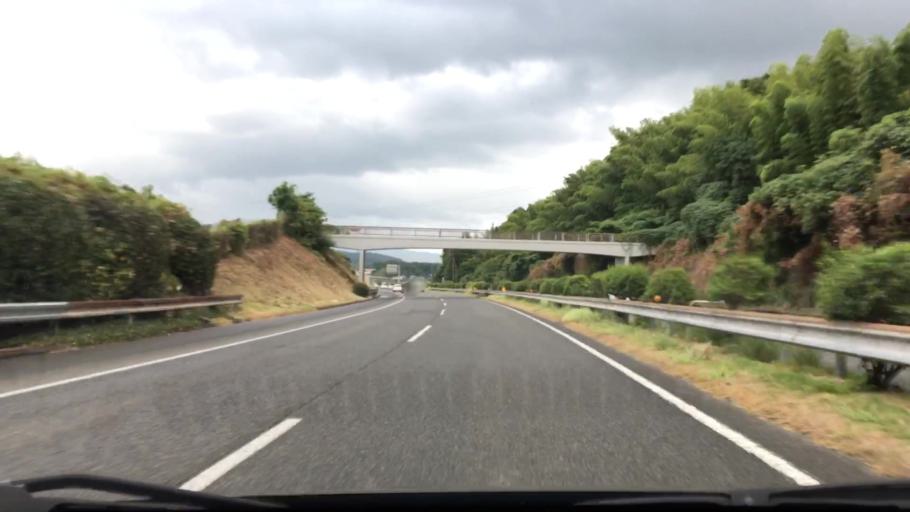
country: JP
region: Fukuoka
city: Miyata
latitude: 33.7464
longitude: 130.5971
